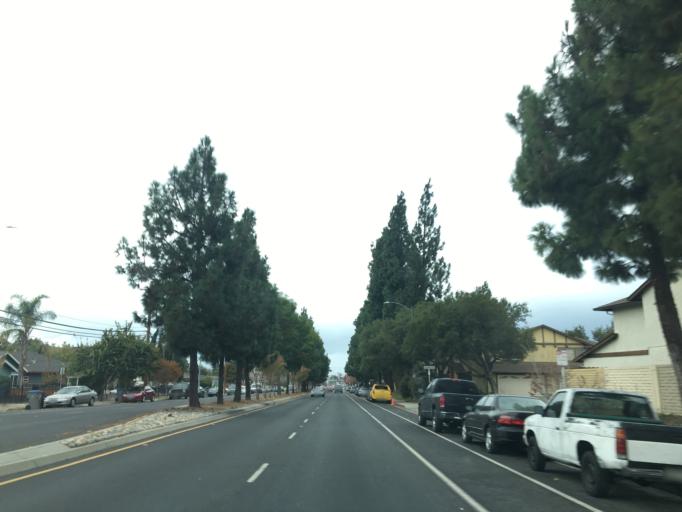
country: US
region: California
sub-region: Santa Clara County
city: Alum Rock
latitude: 37.3686
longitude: -121.8659
